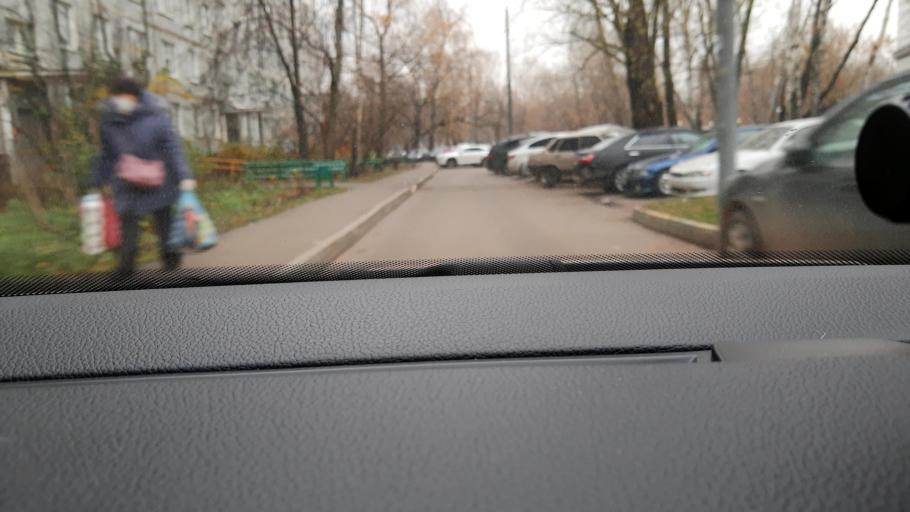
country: RU
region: Moscow
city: Novokuz'minki
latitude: 55.7092
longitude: 37.7840
